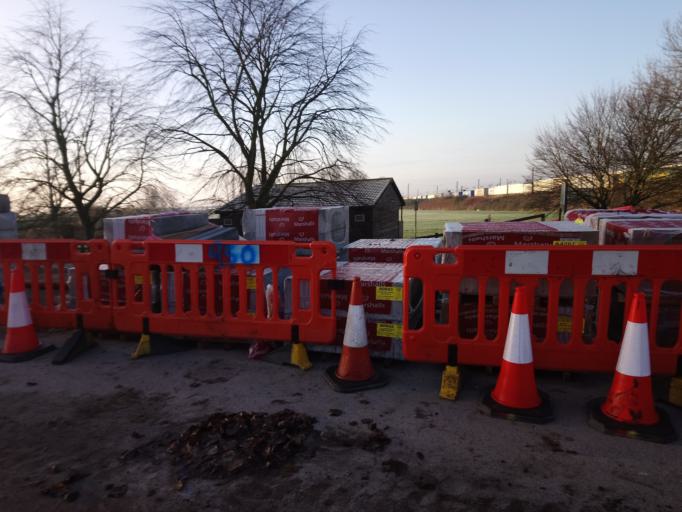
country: GB
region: England
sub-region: Cambridgeshire
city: Ely
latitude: 52.3908
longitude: 0.2681
